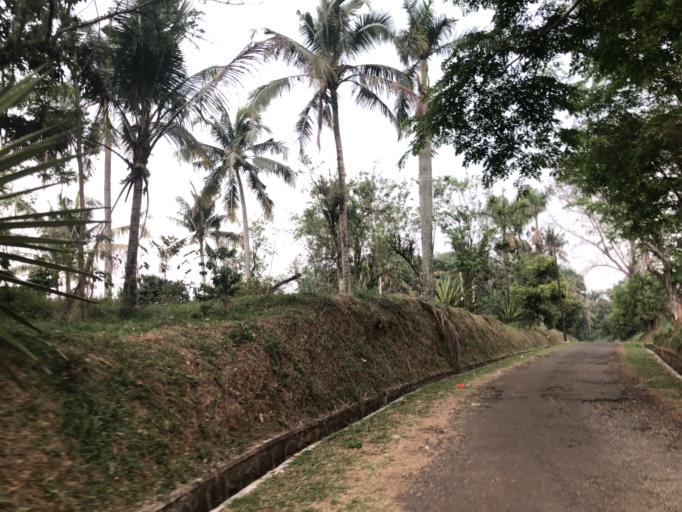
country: ID
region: West Java
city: Ciampea
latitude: -6.5519
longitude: 106.7162
